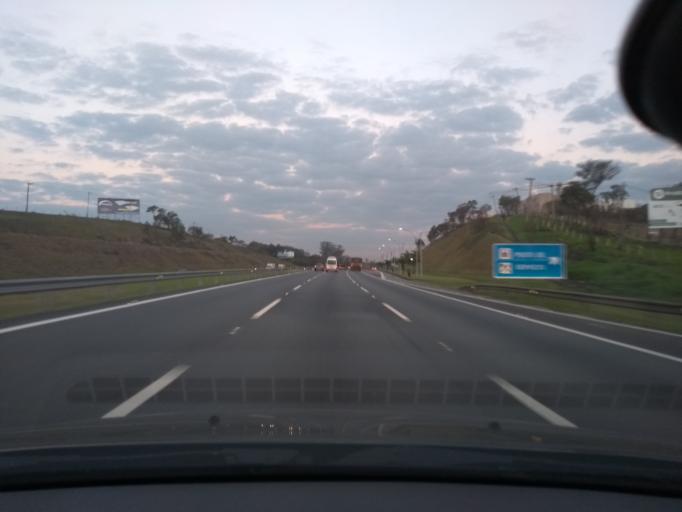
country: BR
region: Sao Paulo
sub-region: Louveira
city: Louveira
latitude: -23.1463
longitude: -46.9651
